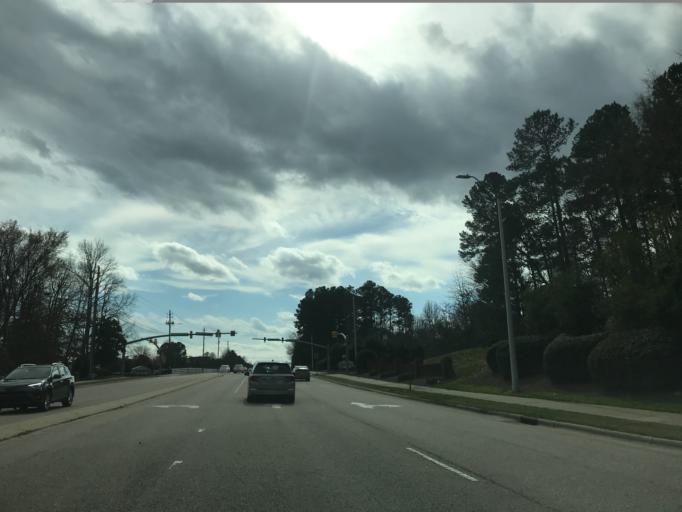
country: US
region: North Carolina
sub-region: Wake County
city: Morrisville
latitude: 35.8043
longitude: -78.8487
